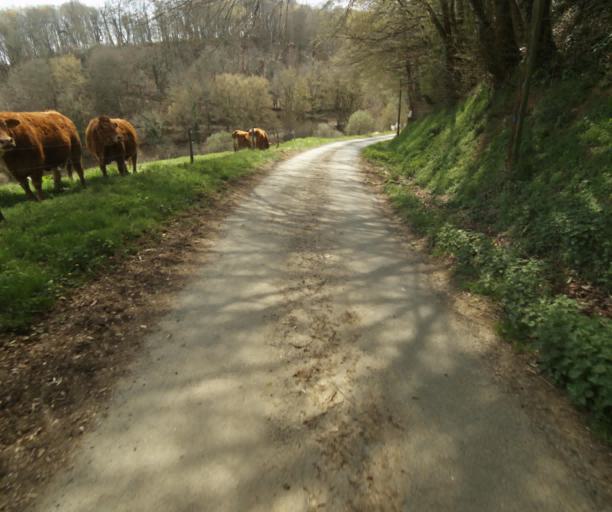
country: FR
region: Limousin
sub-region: Departement de la Correze
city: Naves
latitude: 45.3737
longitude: 1.7826
